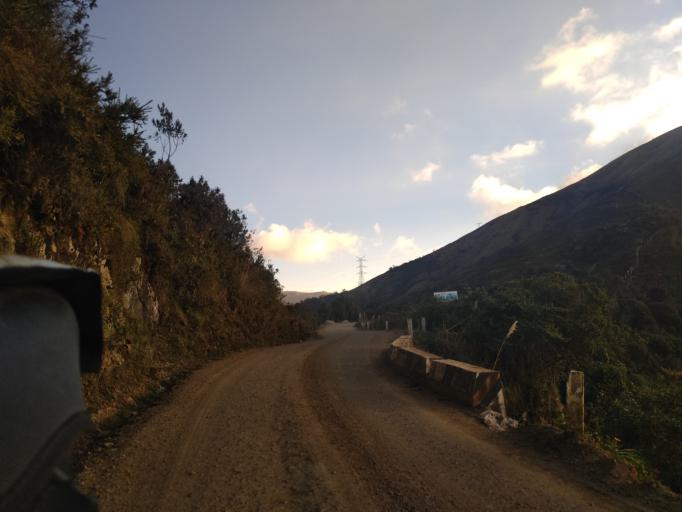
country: PE
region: Amazonas
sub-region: Provincia de Chachapoyas
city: Montevideo
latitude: -6.7135
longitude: -77.8718
